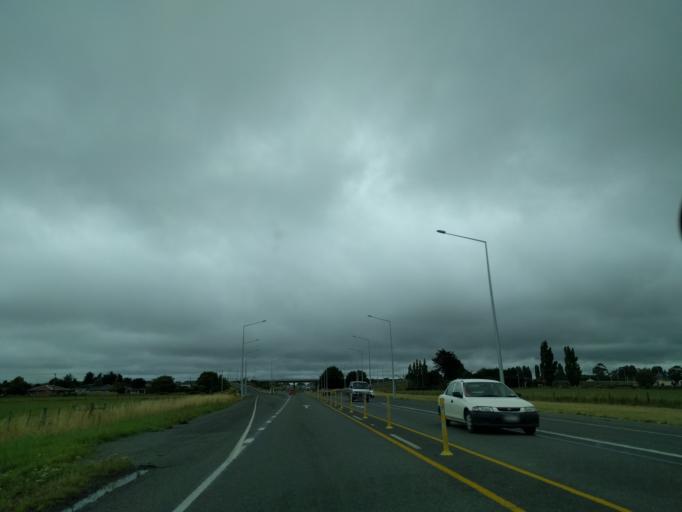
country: NZ
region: Canterbury
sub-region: Waimakariri District
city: Kaiapoi
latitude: -43.3707
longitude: 172.6484
